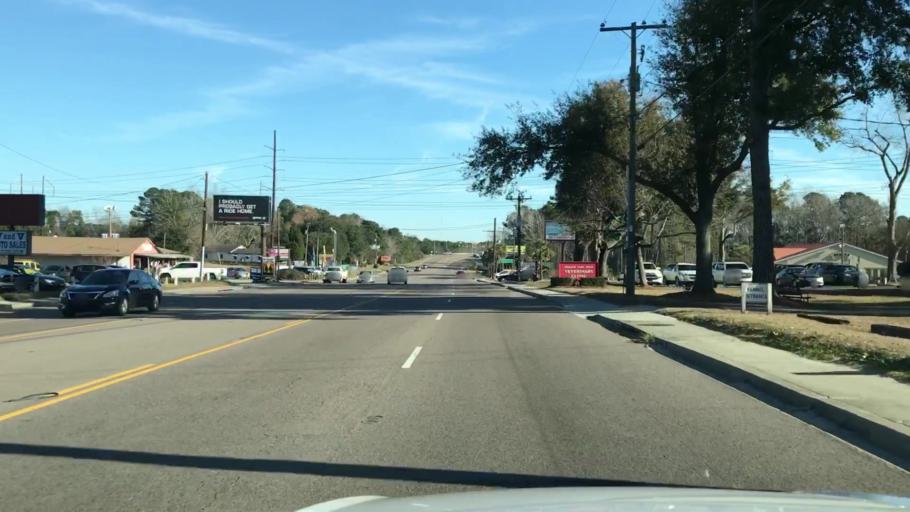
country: US
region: South Carolina
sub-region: Berkeley County
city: Ladson
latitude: 32.9941
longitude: -80.0980
